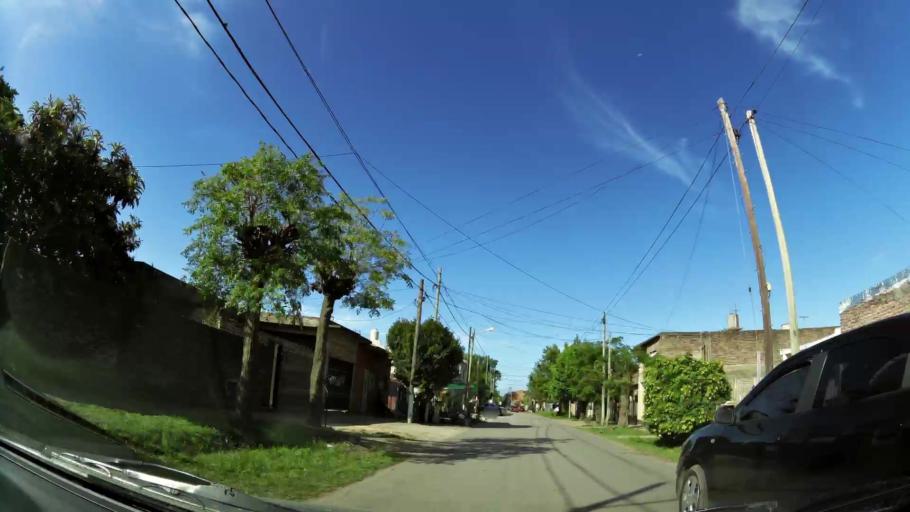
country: AR
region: Buenos Aires
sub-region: Partido de Quilmes
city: Quilmes
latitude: -34.7947
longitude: -58.2322
